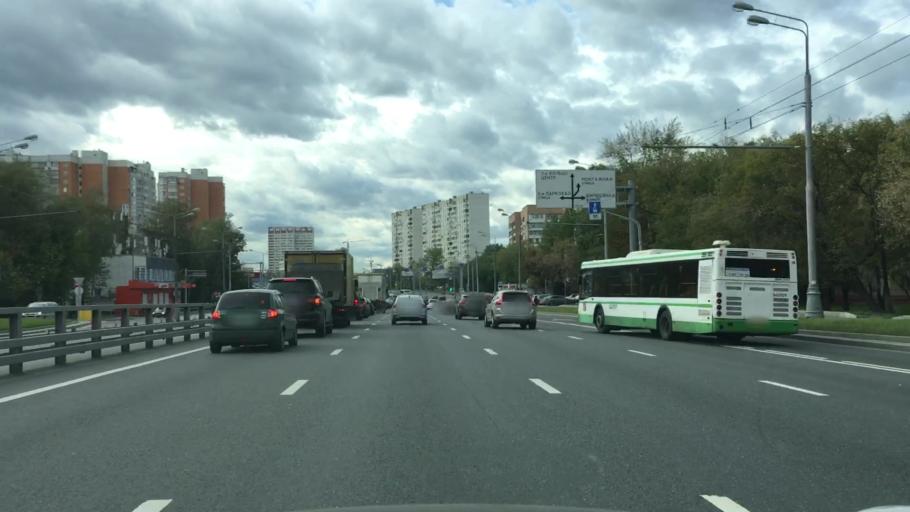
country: RU
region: Moscow
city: Metrogorodok
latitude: 55.8099
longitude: 37.7863
